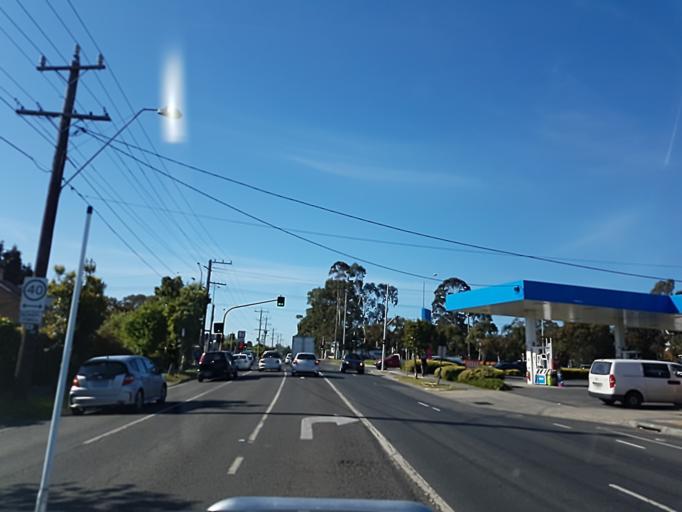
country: AU
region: Victoria
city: Clayton
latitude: -37.9146
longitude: 145.1217
